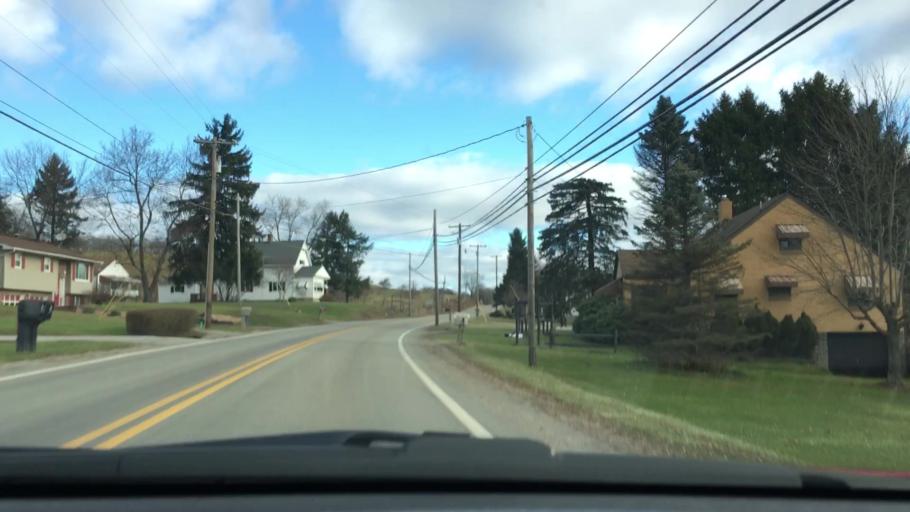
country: US
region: Pennsylvania
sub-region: Armstrong County
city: Orchard Hills
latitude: 40.6003
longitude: -79.5082
